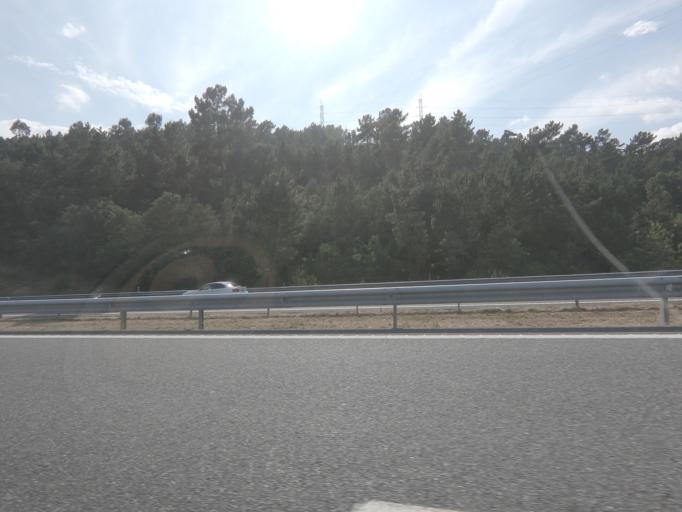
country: ES
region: Galicia
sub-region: Provincia de Ourense
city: Cenlle
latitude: 42.3256
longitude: -8.0771
